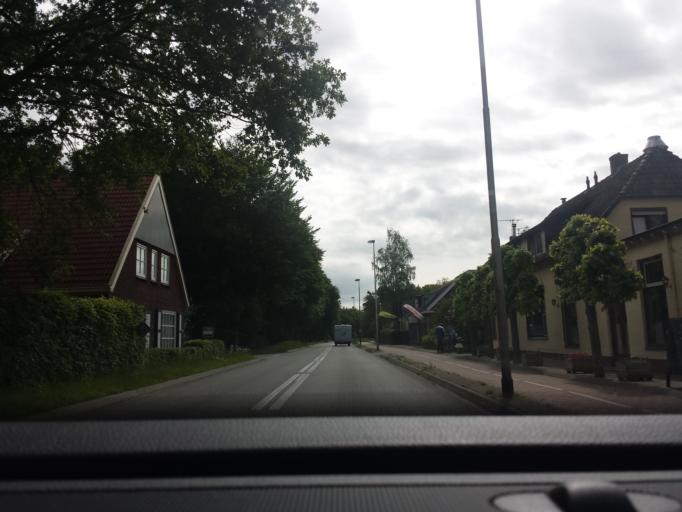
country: NL
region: Gelderland
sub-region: Gemeente Lochem
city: Barchem
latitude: 52.0975
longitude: 6.3873
